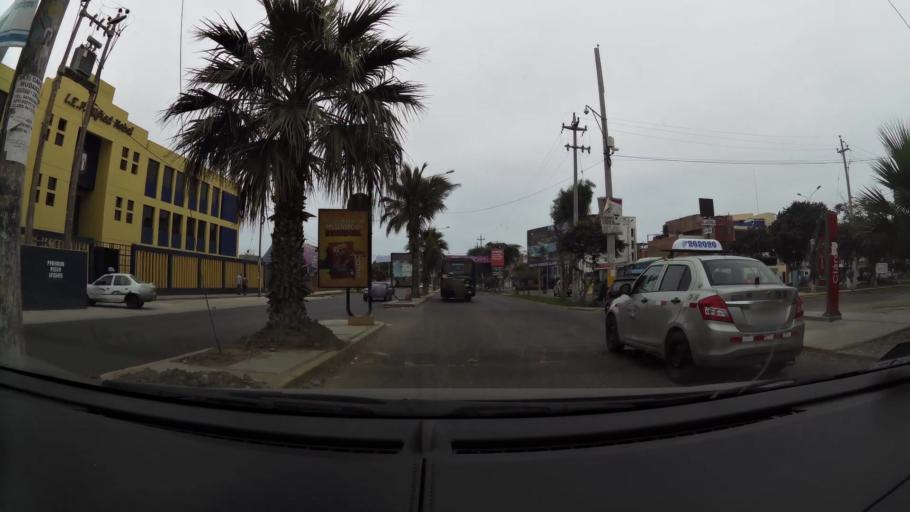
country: PE
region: La Libertad
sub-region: Provincia de Trujillo
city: Buenos Aires
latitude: -8.1308
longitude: -79.0442
